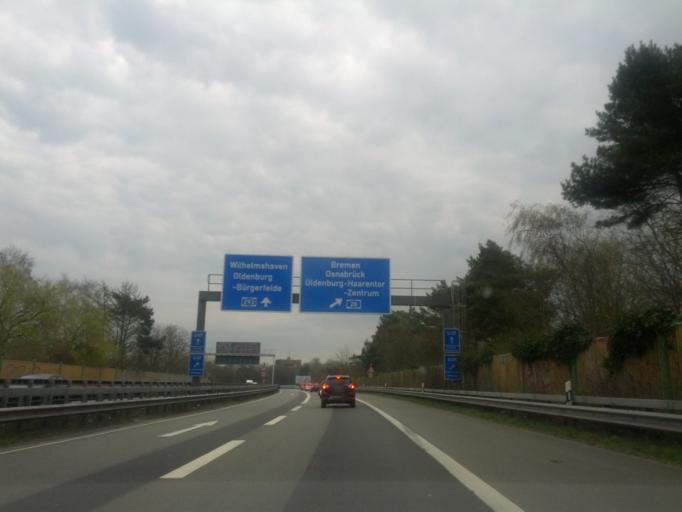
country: DE
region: Lower Saxony
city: Oldenburg
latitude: 53.1533
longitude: 8.1896
